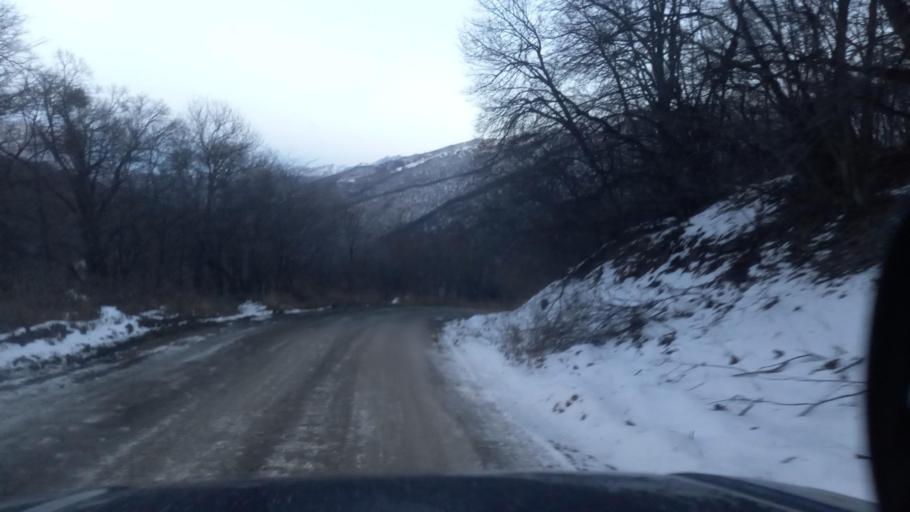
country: RU
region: Ingushetiya
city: Dzhayrakh
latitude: 42.8297
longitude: 44.5843
